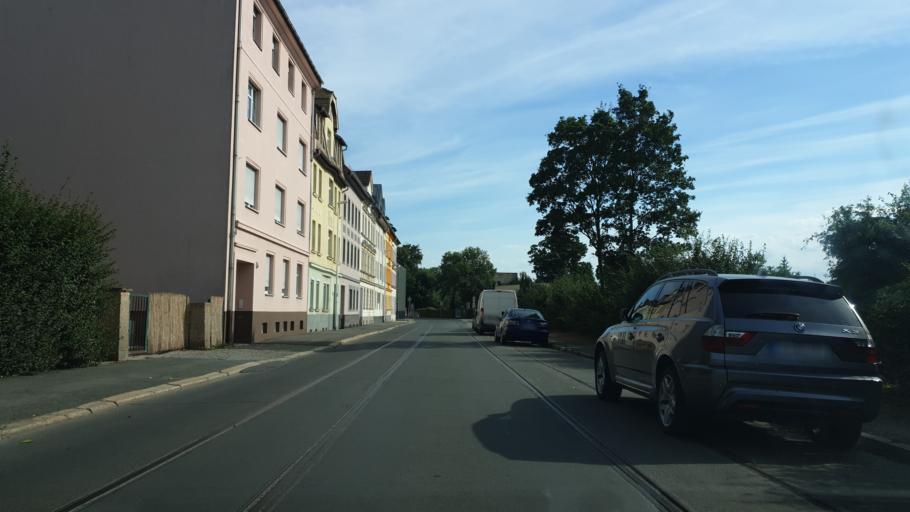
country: DE
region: Thuringia
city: Gera
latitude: 50.8556
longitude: 12.0810
